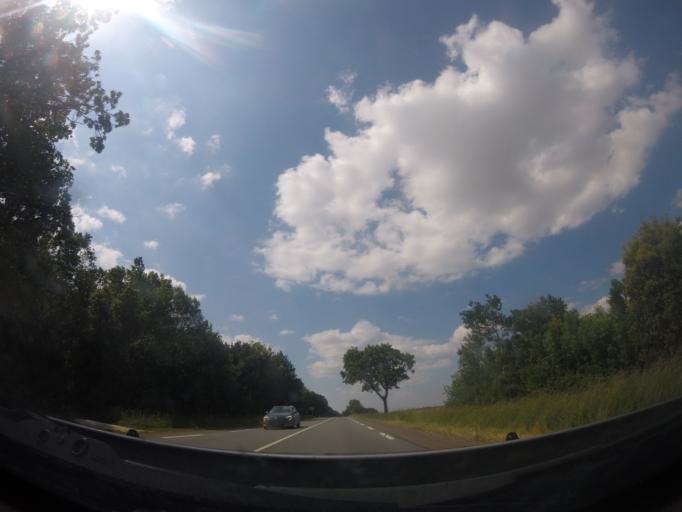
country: FR
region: Poitou-Charentes
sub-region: Departement de la Charente-Maritime
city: Saint-Porchaire
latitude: 45.8419
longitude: -0.8124
